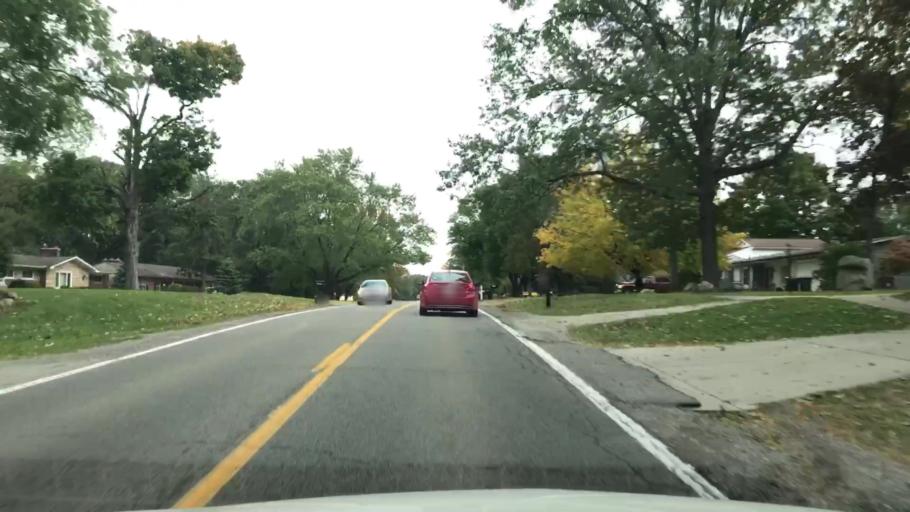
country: US
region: Michigan
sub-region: Macomb County
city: Shelby
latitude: 42.6783
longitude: -83.0663
